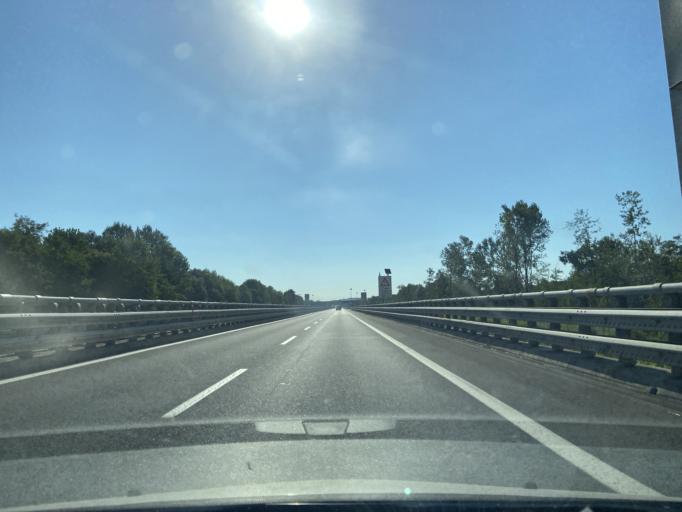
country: IT
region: Piedmont
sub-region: Provincia di Torino
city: Sant'Ambrogio di Torino
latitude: 45.0961
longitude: 7.3836
